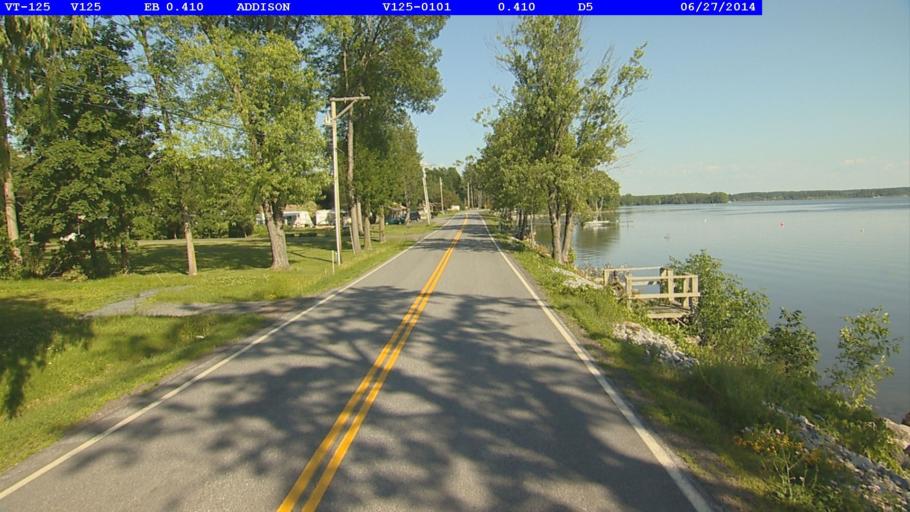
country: US
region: New York
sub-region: Essex County
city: Port Henry
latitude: 44.0335
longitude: -73.4112
